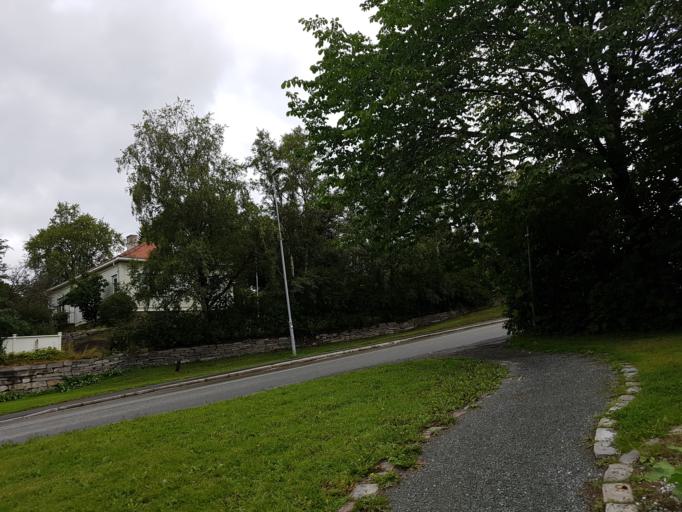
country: NO
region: Sor-Trondelag
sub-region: Trondheim
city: Trondheim
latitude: 63.4167
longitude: 10.4186
